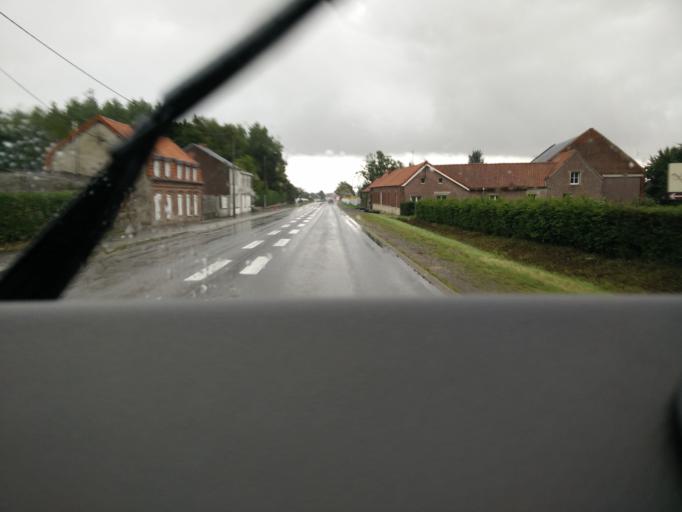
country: FR
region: Nord-Pas-de-Calais
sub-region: Departement du Pas-de-Calais
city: Savy-Berlette
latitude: 50.3556
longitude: 2.4806
